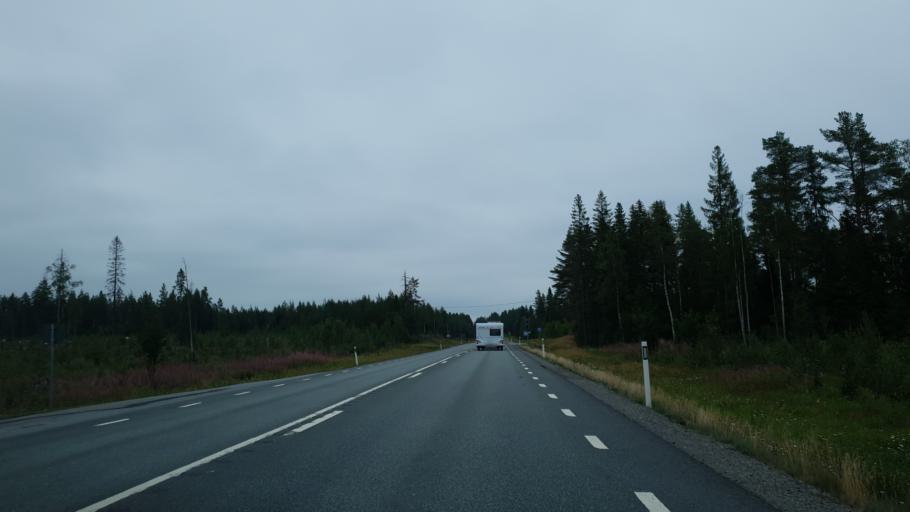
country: SE
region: Vaesterbotten
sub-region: Skelleftea Kommun
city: Burea
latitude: 64.3443
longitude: 21.2844
